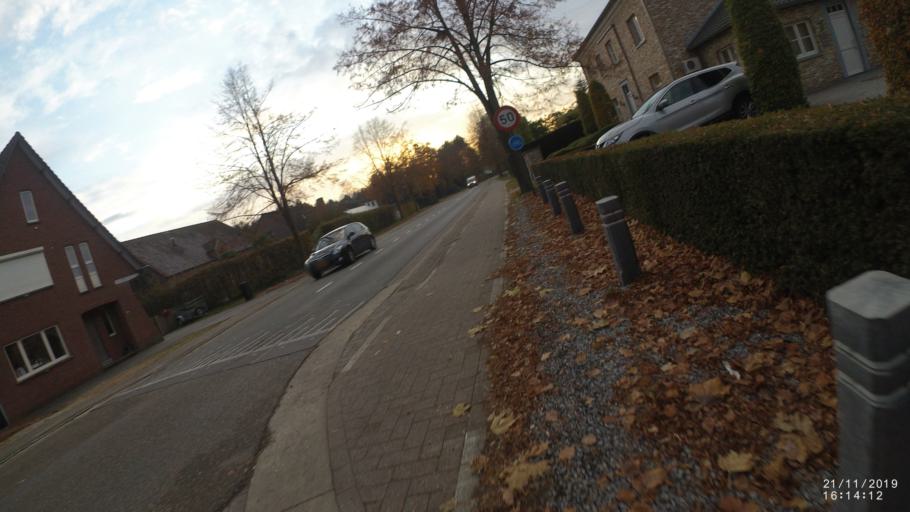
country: BE
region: Flanders
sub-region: Provincie Limburg
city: Zonhoven
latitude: 50.9916
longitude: 5.3531
